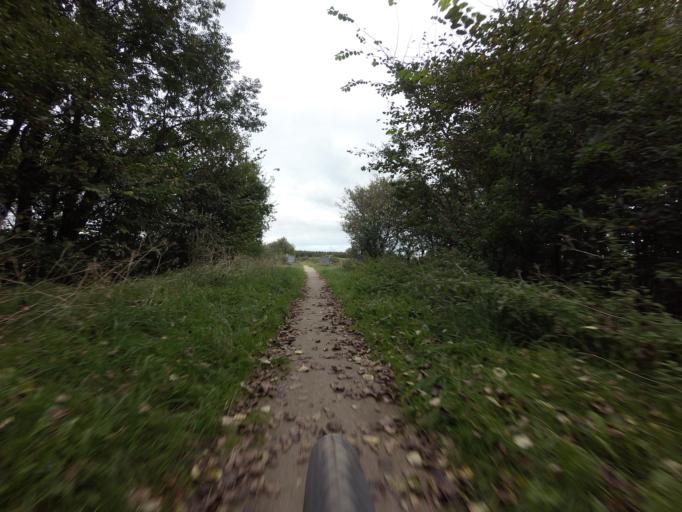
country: DK
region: South Denmark
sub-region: Billund Kommune
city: Billund
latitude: 55.8171
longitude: 9.0303
